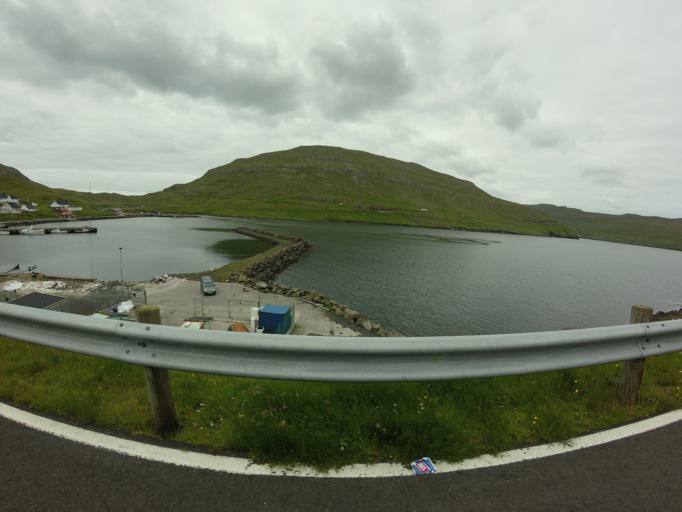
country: FO
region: Suduroy
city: Vagur
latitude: 61.4453
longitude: -6.7676
